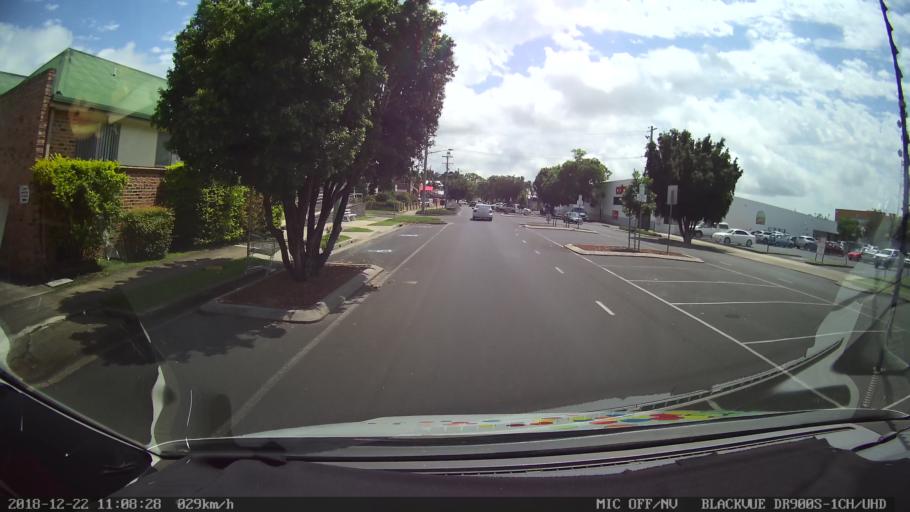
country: AU
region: New South Wales
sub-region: Clarence Valley
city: Grafton
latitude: -29.6892
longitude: 152.9313
